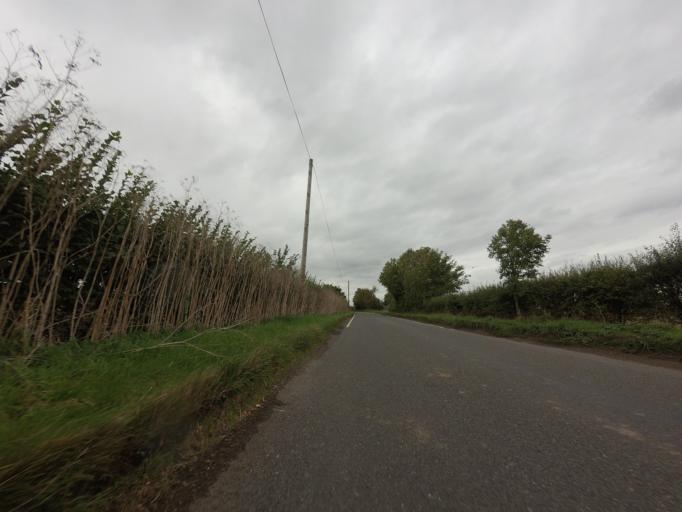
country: GB
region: England
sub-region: Cambridgeshire
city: Harston
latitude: 52.1027
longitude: 0.0553
